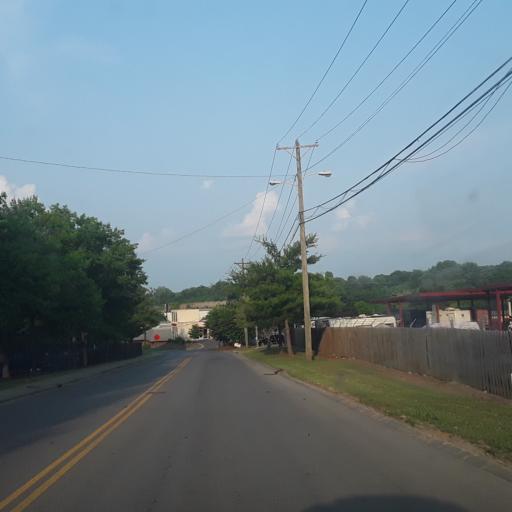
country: US
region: Tennessee
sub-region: Williamson County
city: Brentwood Estates
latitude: 36.0419
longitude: -86.7169
